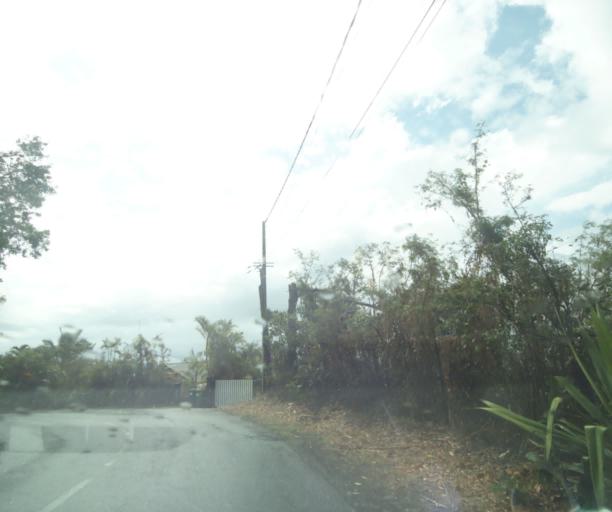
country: RE
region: Reunion
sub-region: Reunion
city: Saint-Paul
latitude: -21.0085
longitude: 55.3170
